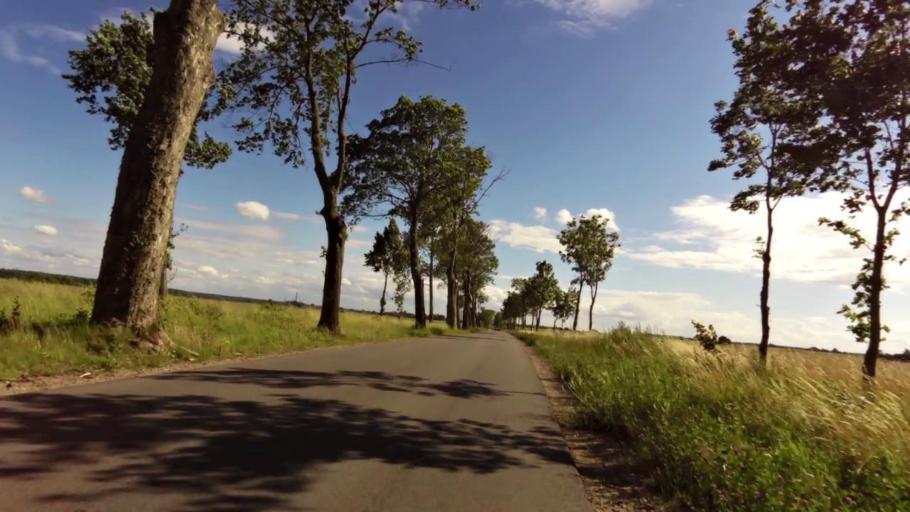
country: PL
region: West Pomeranian Voivodeship
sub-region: Powiat slawienski
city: Slawno
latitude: 54.4498
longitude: 16.7374
